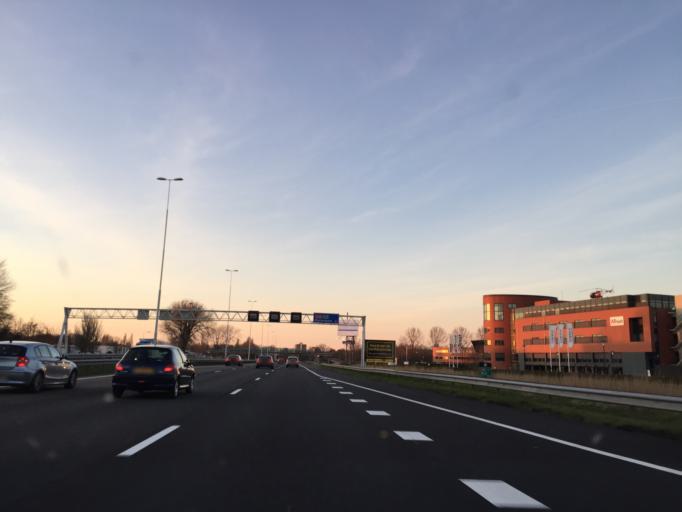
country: NL
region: South Holland
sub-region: Gemeente Dordrecht
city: Dordrecht
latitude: 51.7739
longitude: 4.6495
